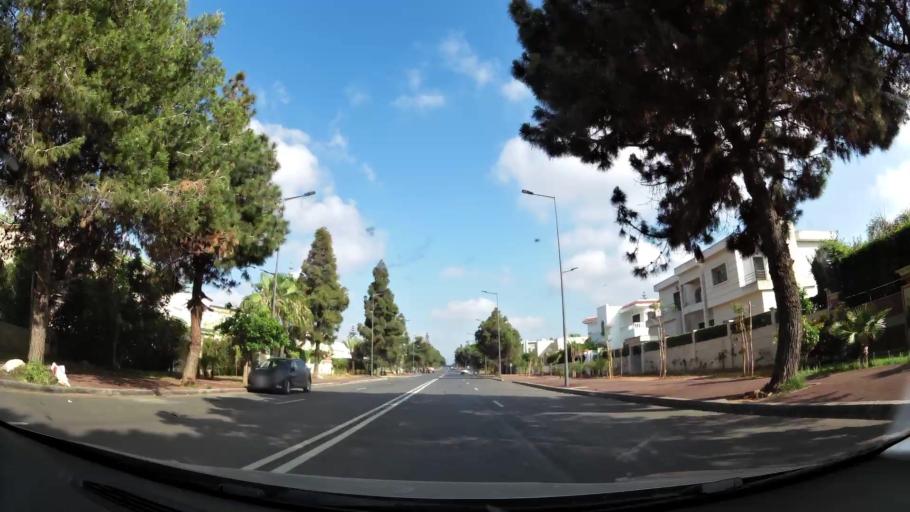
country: MA
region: Rabat-Sale-Zemmour-Zaer
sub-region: Skhirate-Temara
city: Temara
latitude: 33.9608
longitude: -6.8639
